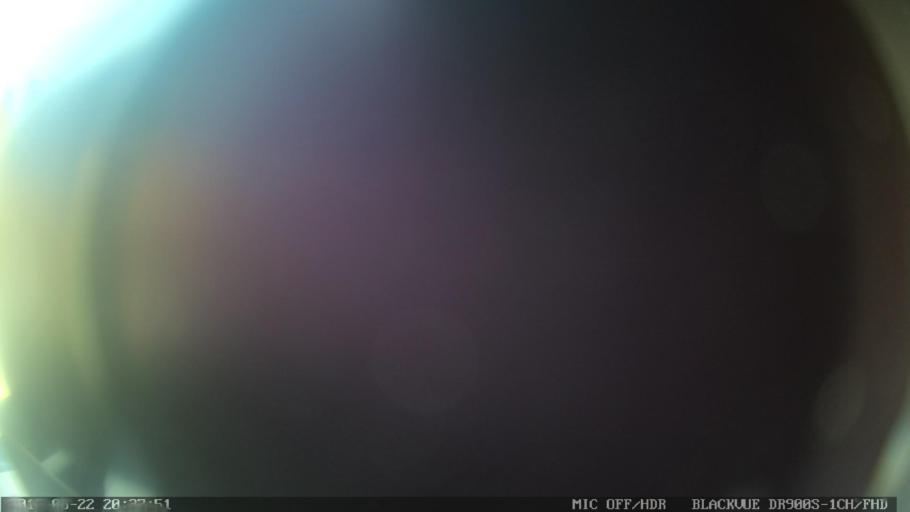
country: PT
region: Portalegre
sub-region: Nisa
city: Nisa
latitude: 39.6783
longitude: -7.7400
